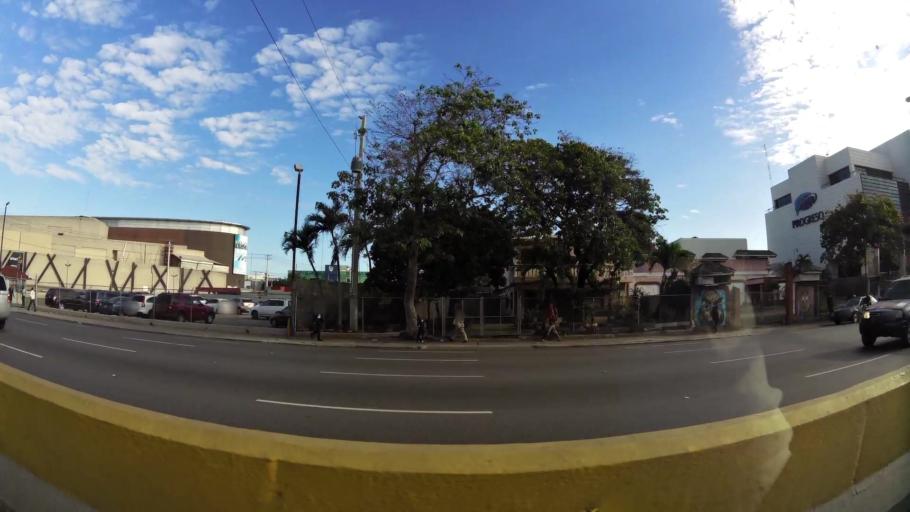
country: DO
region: Nacional
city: San Carlos
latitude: 18.4818
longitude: -69.9099
